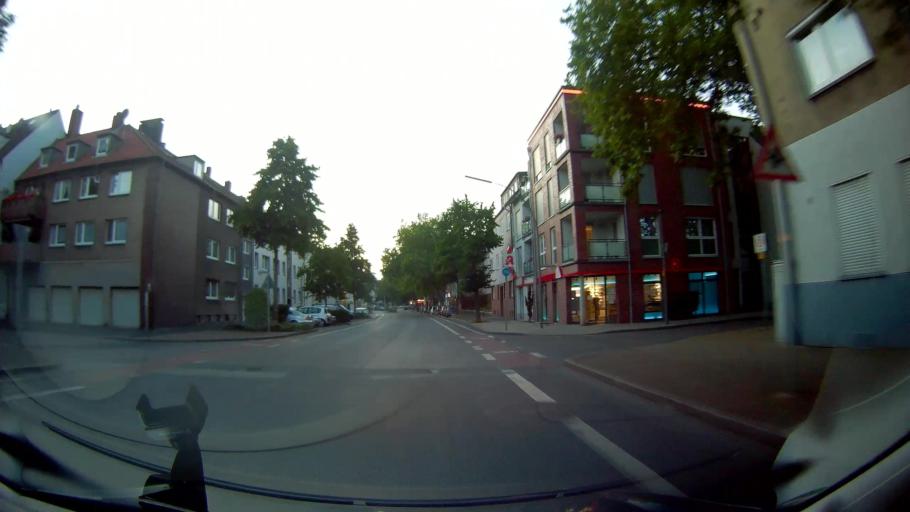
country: DE
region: North Rhine-Westphalia
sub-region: Regierungsbezirk Munster
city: Gladbeck
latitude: 51.5297
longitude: 7.0272
